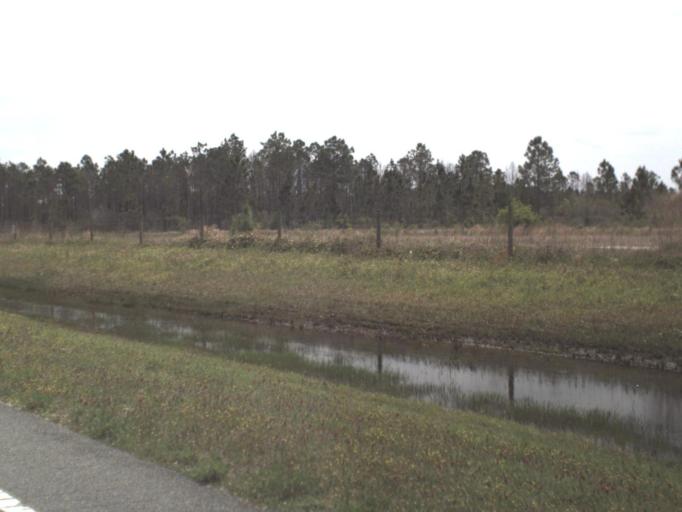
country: US
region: Florida
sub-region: Escambia County
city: Myrtle Grove
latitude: 30.4031
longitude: -87.3337
